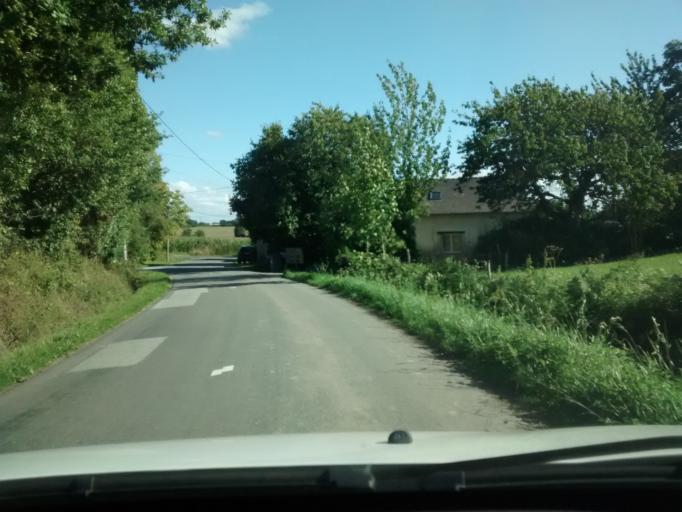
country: FR
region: Brittany
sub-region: Departement d'Ille-et-Vilaine
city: Chantepie
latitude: 48.0925
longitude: -1.5850
